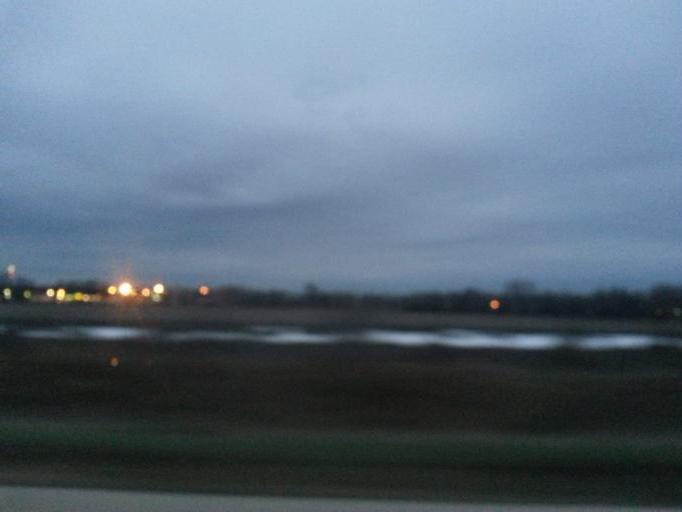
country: US
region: Iowa
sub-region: Black Hawk County
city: Elk Run Heights
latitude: 42.4539
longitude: -92.2477
